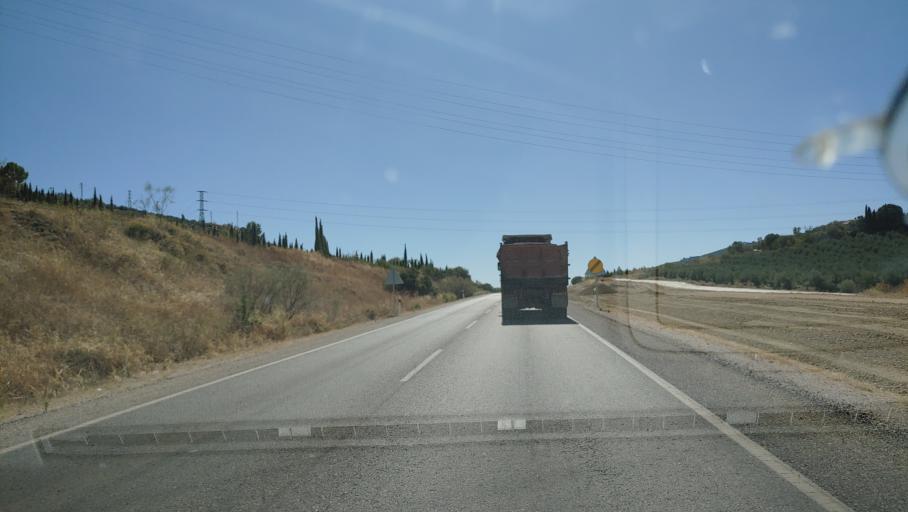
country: ES
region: Andalusia
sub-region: Provincia de Jaen
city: Villanueva del Arzobispo
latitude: 38.1597
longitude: -2.9970
